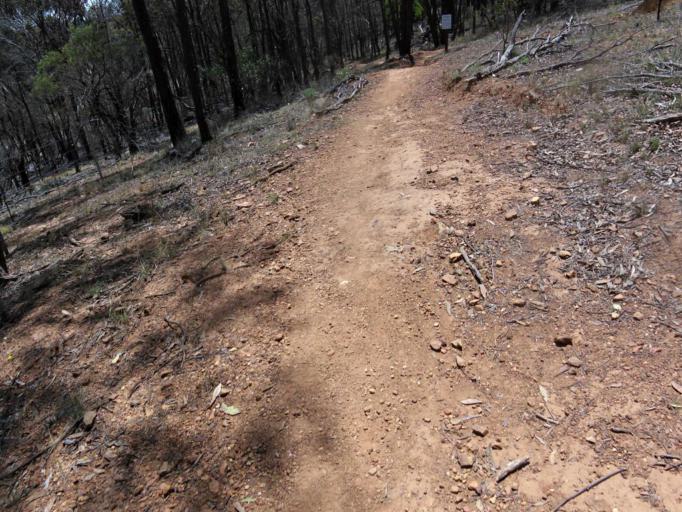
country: AU
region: Australian Capital Territory
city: Kaleen
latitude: -35.1384
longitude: 149.1480
